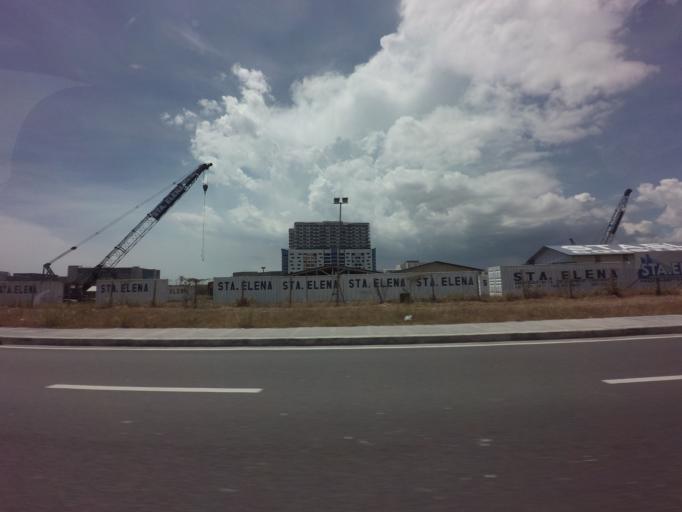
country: PH
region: Metro Manila
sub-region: Makati City
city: Makati City
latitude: 14.5176
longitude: 120.9882
